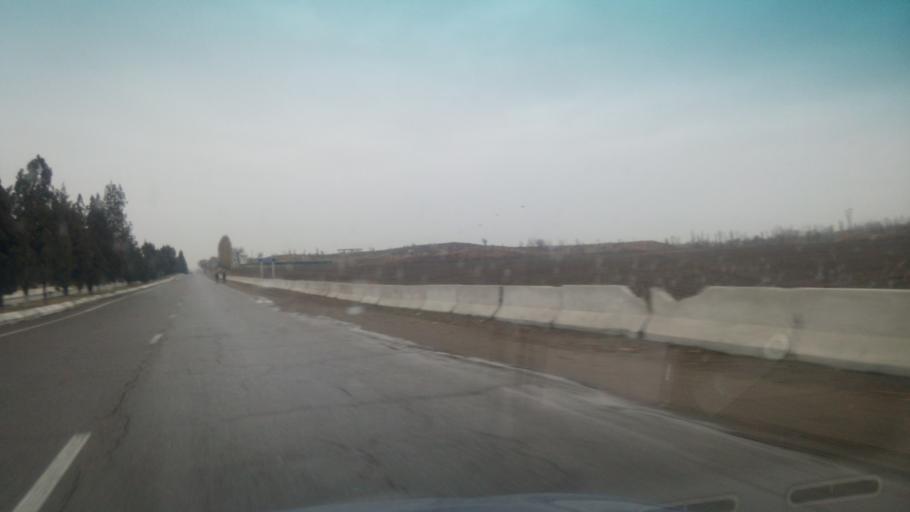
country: UZ
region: Toshkent
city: Zafar
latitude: 41.0423
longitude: 68.8839
